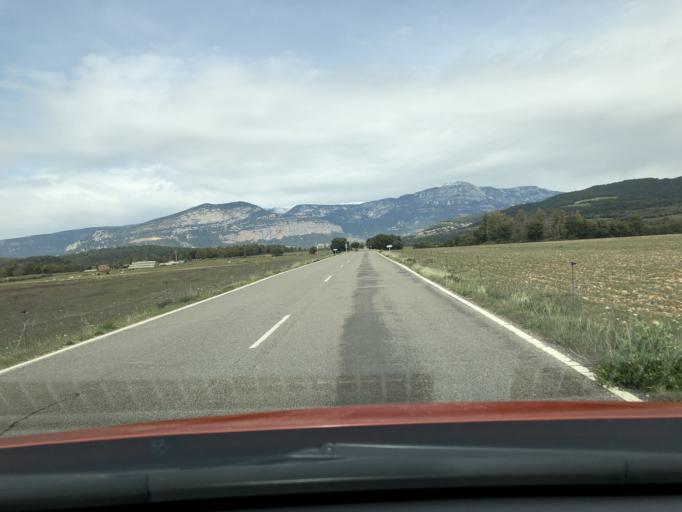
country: ES
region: Catalonia
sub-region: Provincia de Lleida
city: Solsona
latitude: 42.0674
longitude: 1.5108
